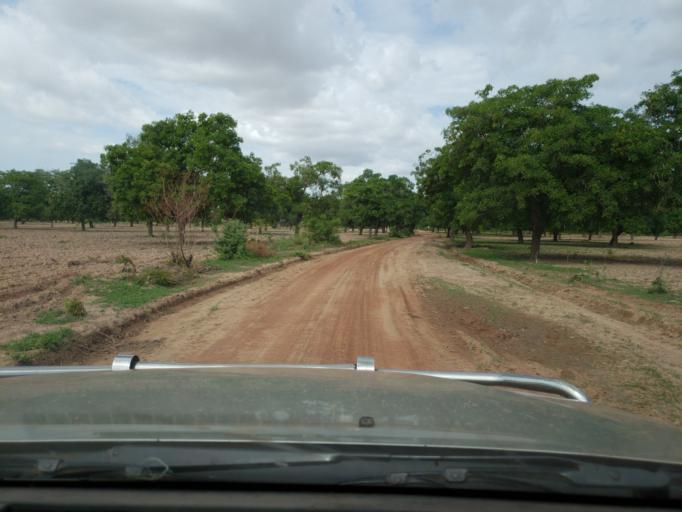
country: ML
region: Segou
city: Bla
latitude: 12.7084
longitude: -5.7089
